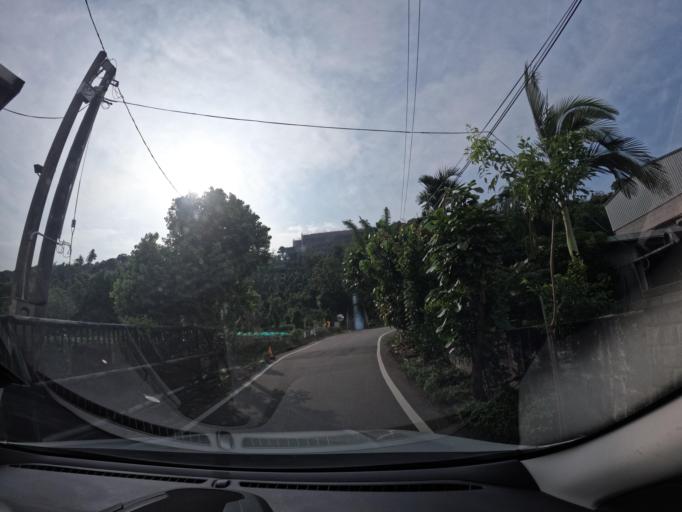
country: TW
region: Taiwan
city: Daxi
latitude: 24.9275
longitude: 121.3060
